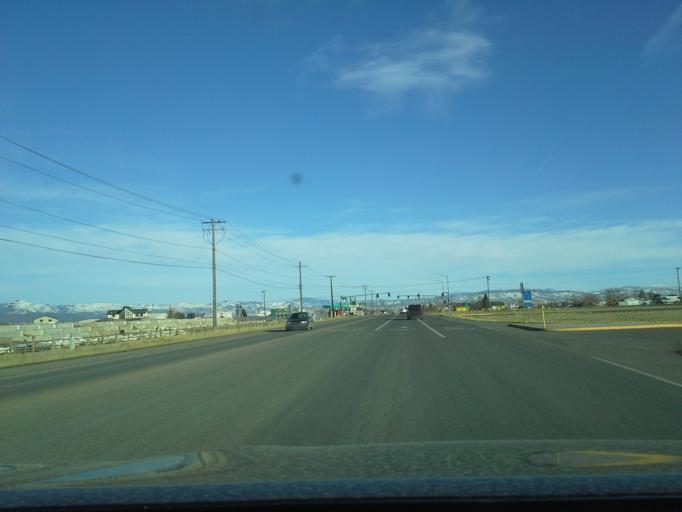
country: US
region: Montana
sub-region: Lewis and Clark County
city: Helena Valley Southeast
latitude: 46.6168
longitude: -111.9391
